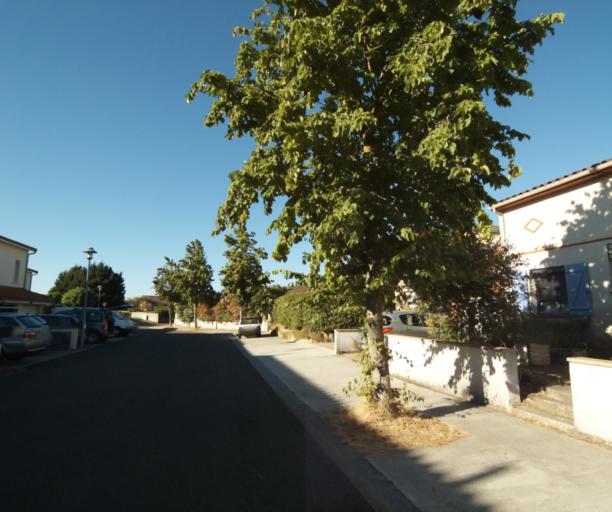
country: FR
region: Midi-Pyrenees
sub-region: Departement de la Haute-Garonne
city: Castanet-Tolosan
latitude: 43.5188
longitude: 1.5140
